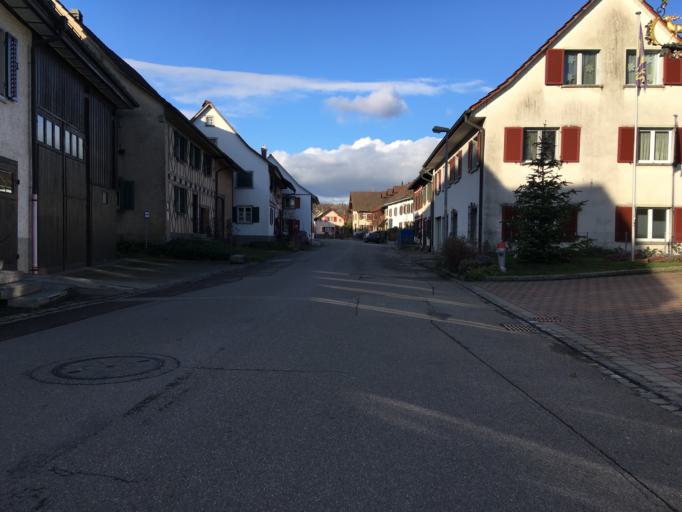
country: CH
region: Schaffhausen
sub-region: Bezirk Stein
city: Ramsen
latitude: 47.7085
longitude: 8.8097
